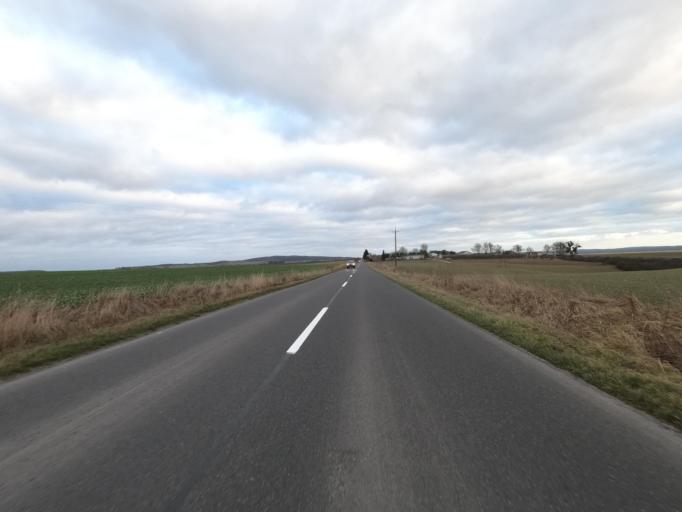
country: PL
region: Greater Poland Voivodeship
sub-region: Powiat pilski
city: Bialosliwie
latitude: 53.1101
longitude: 17.1440
